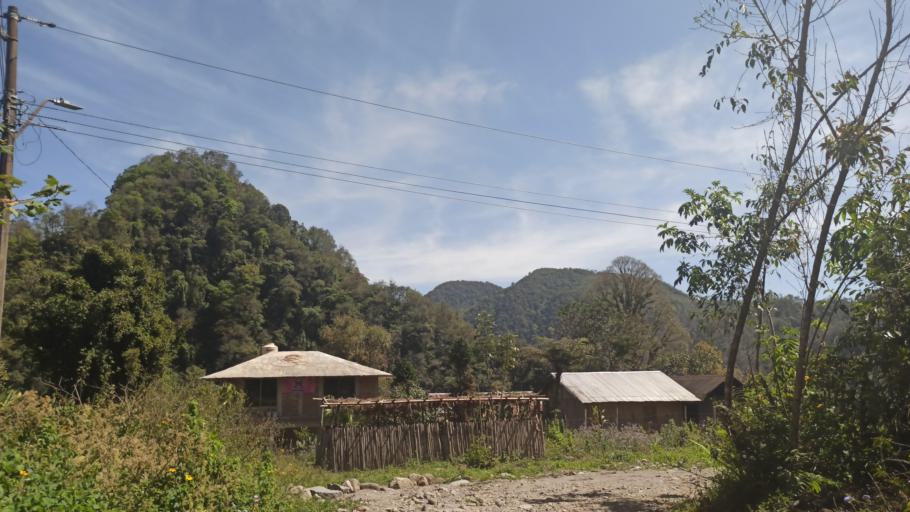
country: MX
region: Veracruz
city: Xocotla
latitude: 18.9798
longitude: -97.0885
